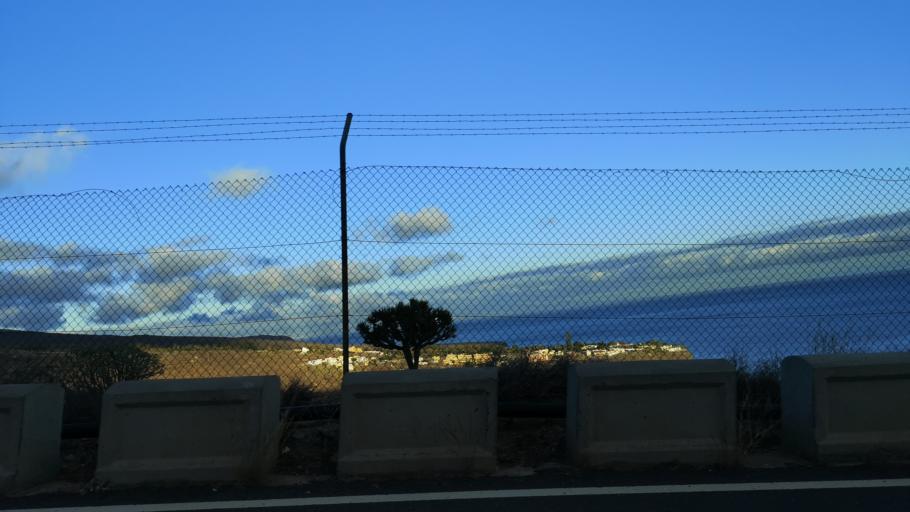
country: ES
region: Canary Islands
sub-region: Provincia de Santa Cruz de Tenerife
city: Alajero
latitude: 28.0311
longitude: -17.2058
